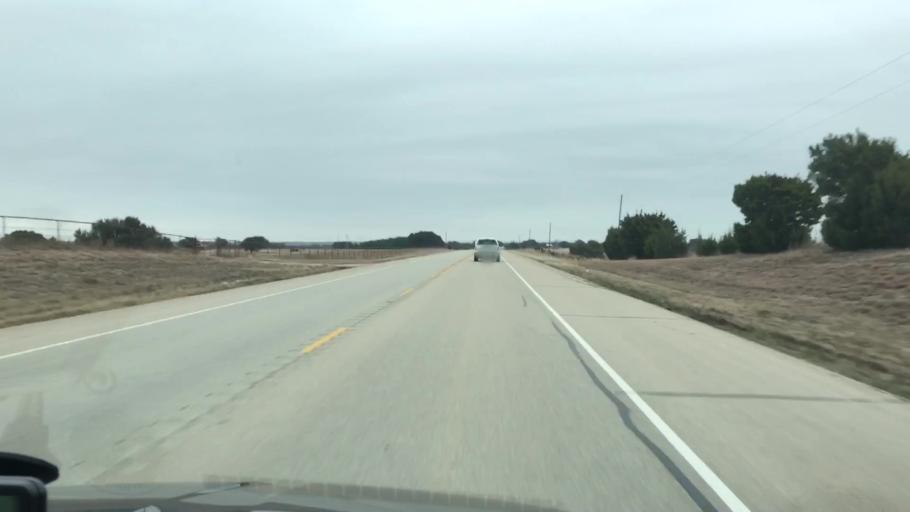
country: US
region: Texas
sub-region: Hamilton County
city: Hico
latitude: 31.8960
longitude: -98.0934
